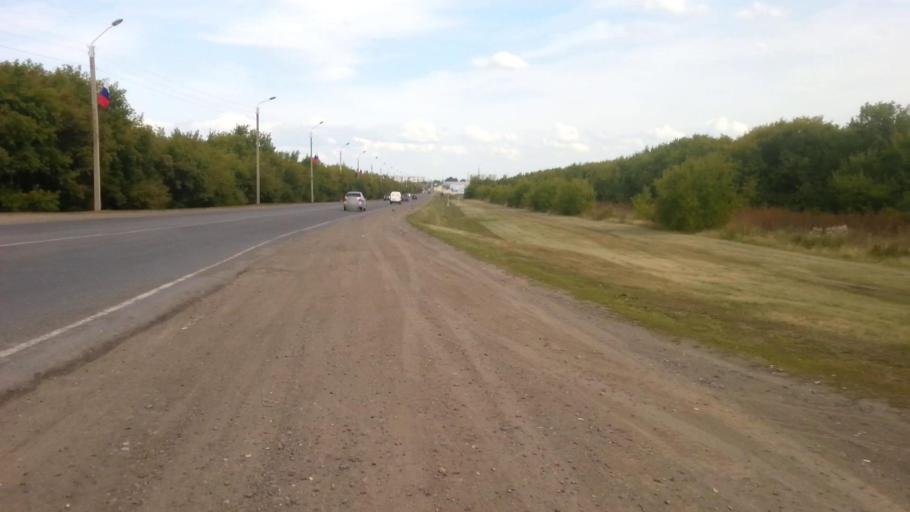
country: RU
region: Altai Krai
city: Novosilikatnyy
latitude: 53.3507
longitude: 83.5970
